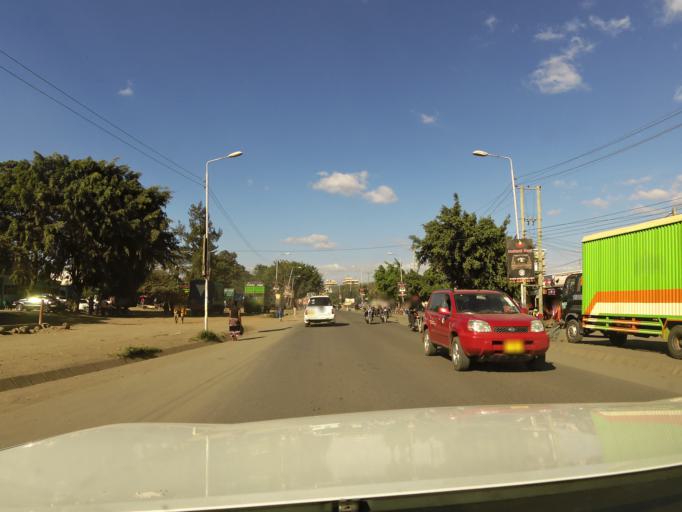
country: TZ
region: Arusha
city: Arusha
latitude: -3.3753
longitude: 36.6756
